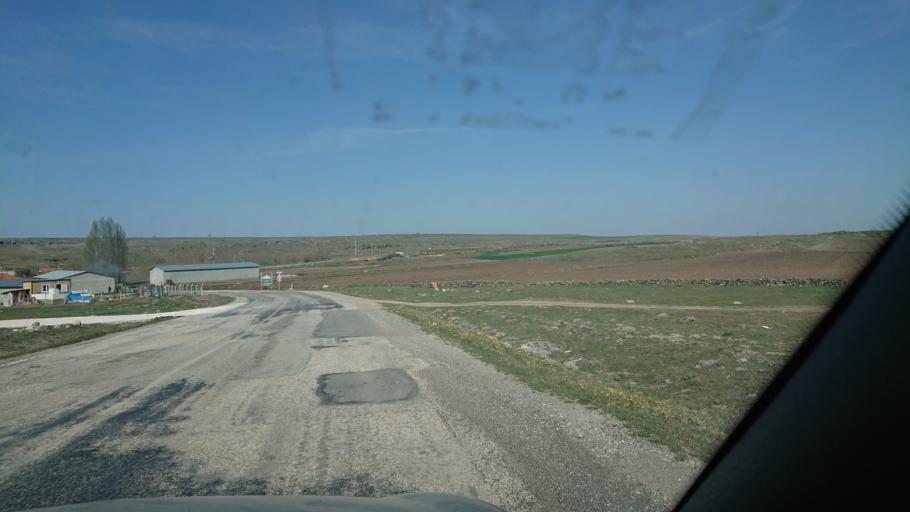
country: TR
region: Eskisehir
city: Eskisehir
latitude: 39.6758
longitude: 30.4839
